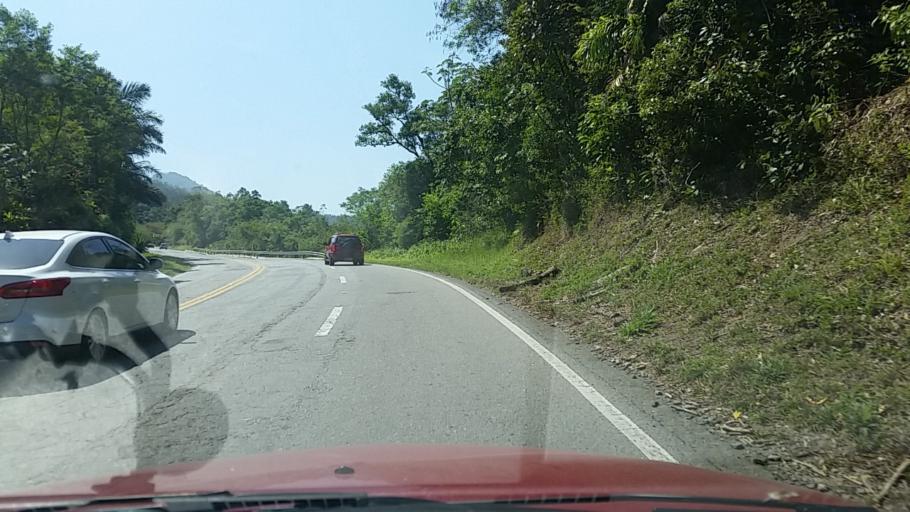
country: BR
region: Sao Paulo
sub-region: Miracatu
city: Miracatu
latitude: -24.3815
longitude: -47.5049
